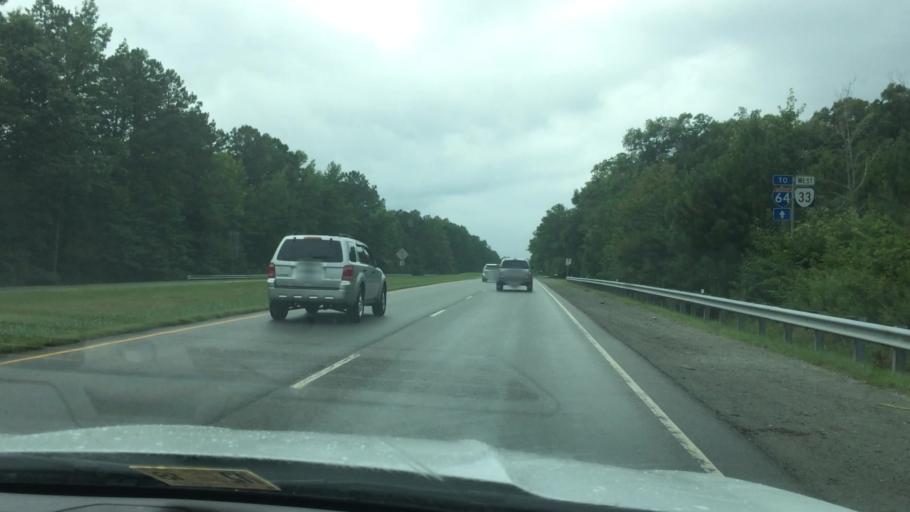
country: US
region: Virginia
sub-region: King William County
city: West Point
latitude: 37.5007
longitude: -76.8752
